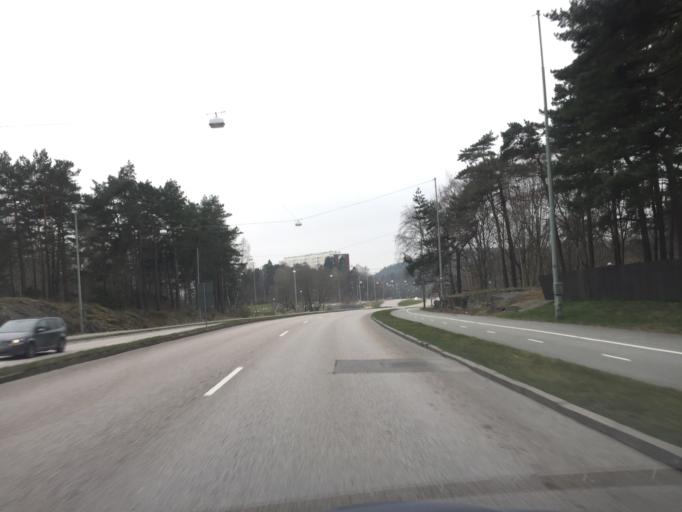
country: SE
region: Vaestra Goetaland
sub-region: Goteborg
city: Eriksbo
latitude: 57.7444
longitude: 12.0323
